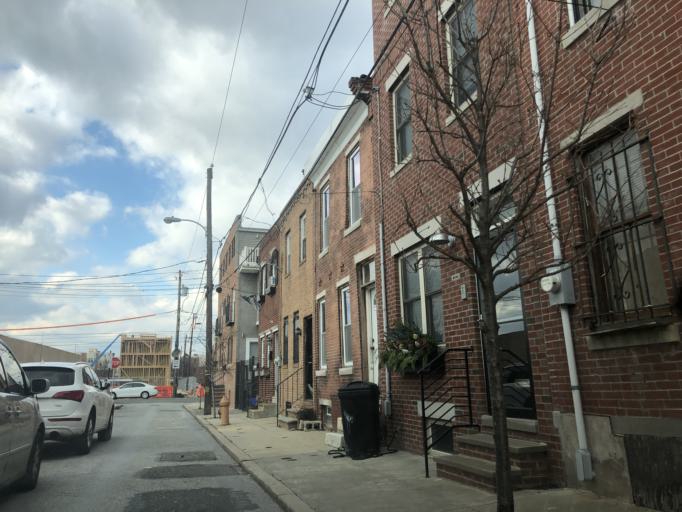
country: US
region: Pennsylvania
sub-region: Philadelphia County
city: Philadelphia
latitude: 39.9400
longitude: -75.1775
